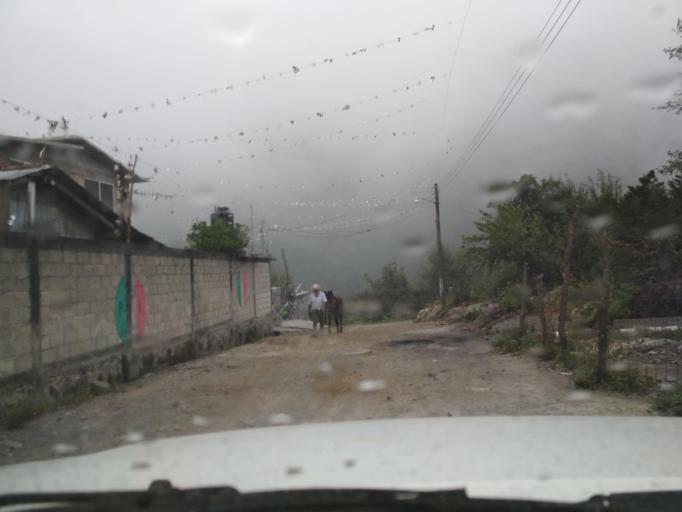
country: MX
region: Veracruz
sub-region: Mariano Escobedo
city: San Isidro el Berro
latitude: 18.9534
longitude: -97.1835
